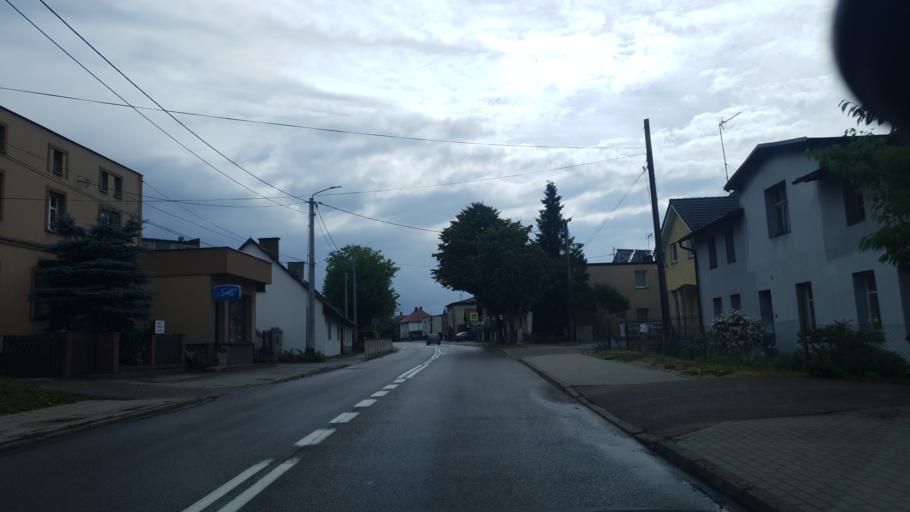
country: PL
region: Pomeranian Voivodeship
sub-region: Powiat kartuski
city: Kartuzy
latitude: 54.3287
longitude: 18.1957
